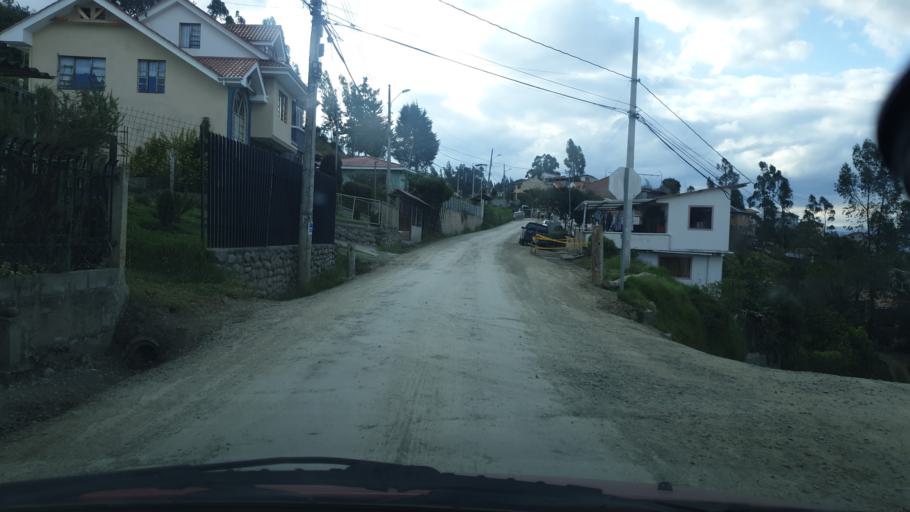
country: EC
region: Azuay
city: Cuenca
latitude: -2.9217
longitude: -78.9747
